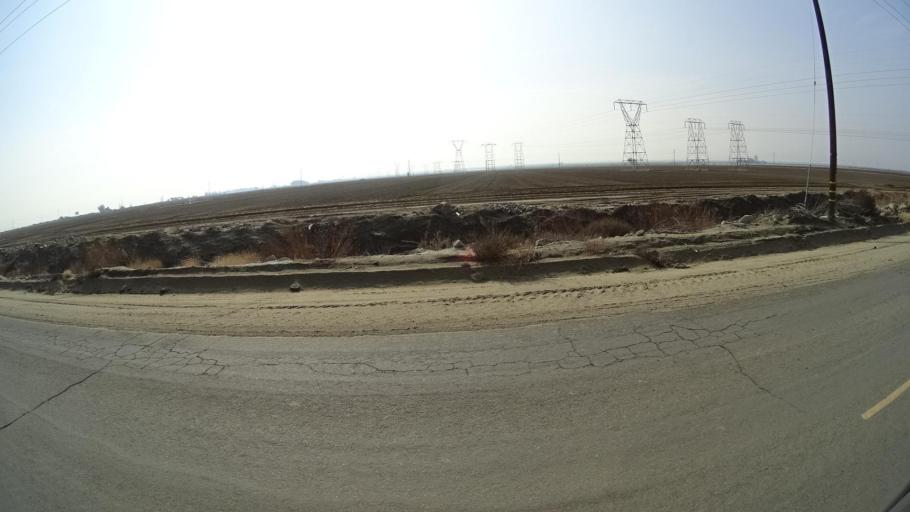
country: US
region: California
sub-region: Kern County
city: Arvin
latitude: 35.0928
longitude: -118.8873
